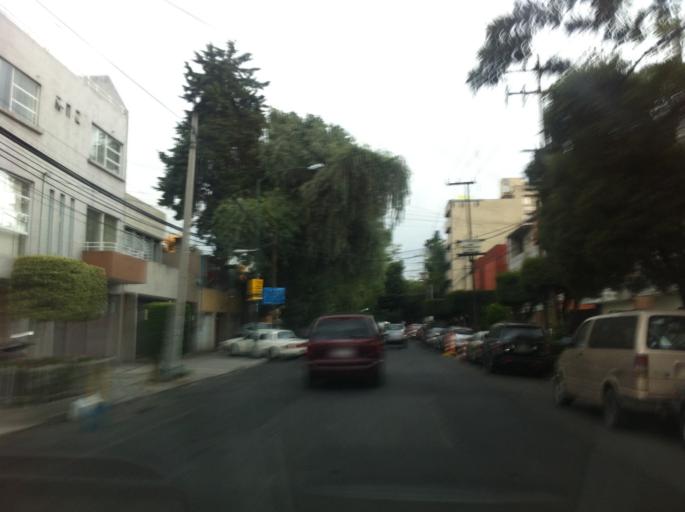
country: MX
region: Mexico City
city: Colonia del Valle
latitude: 19.3701
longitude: -99.1667
